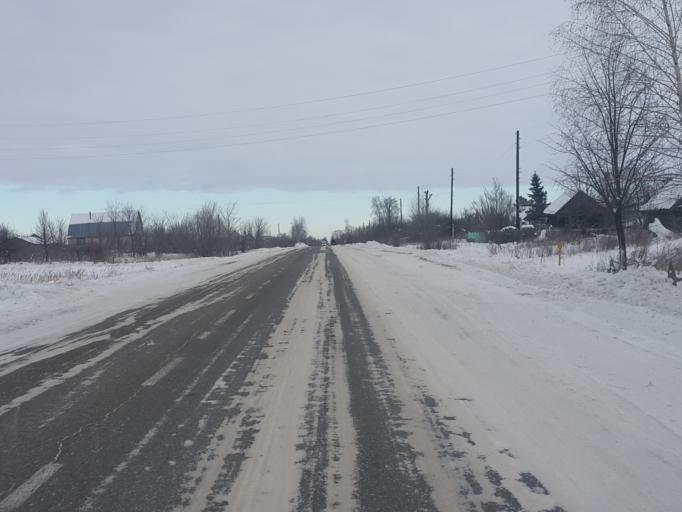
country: RU
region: Tambov
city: Platonovka
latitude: 52.8604
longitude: 41.8399
